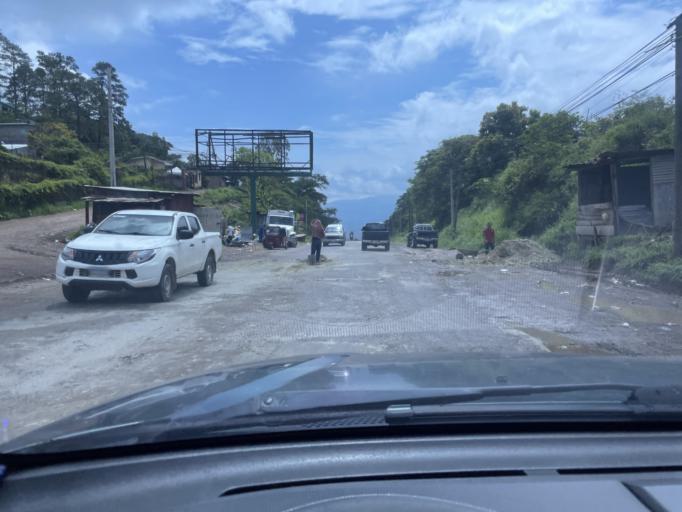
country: HN
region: Francisco Morazan
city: Rio Abajo
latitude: 14.1384
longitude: -87.2324
